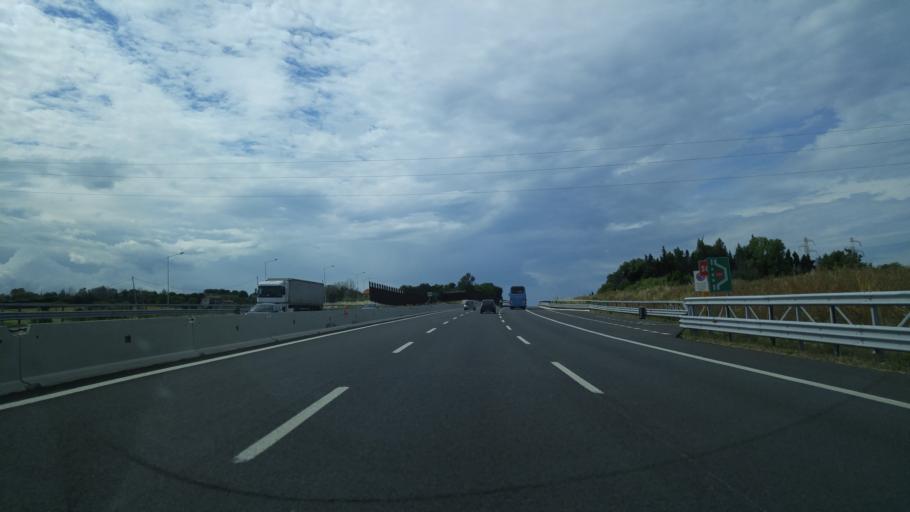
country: IT
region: Emilia-Romagna
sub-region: Provincia di Rimini
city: Rivazzurra
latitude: 44.0158
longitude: 12.5882
